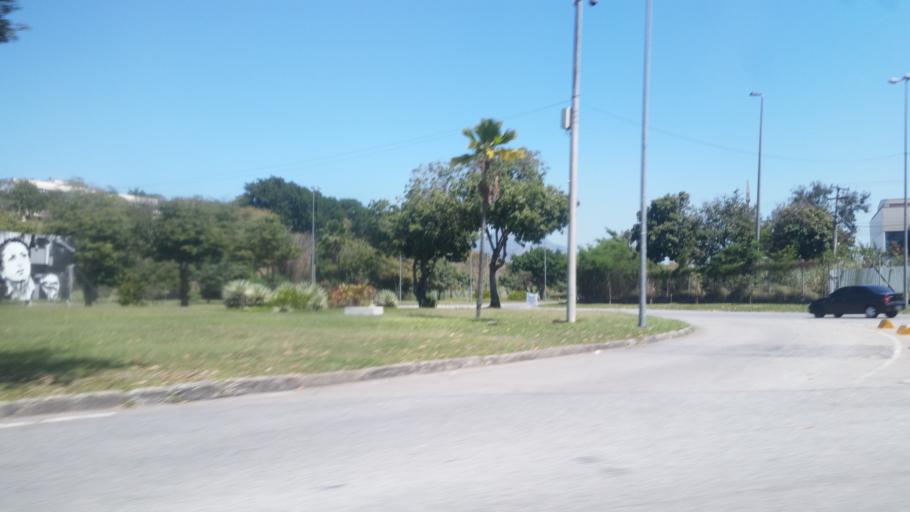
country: BR
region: Rio de Janeiro
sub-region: Rio De Janeiro
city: Rio de Janeiro
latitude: -22.8609
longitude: -43.2270
